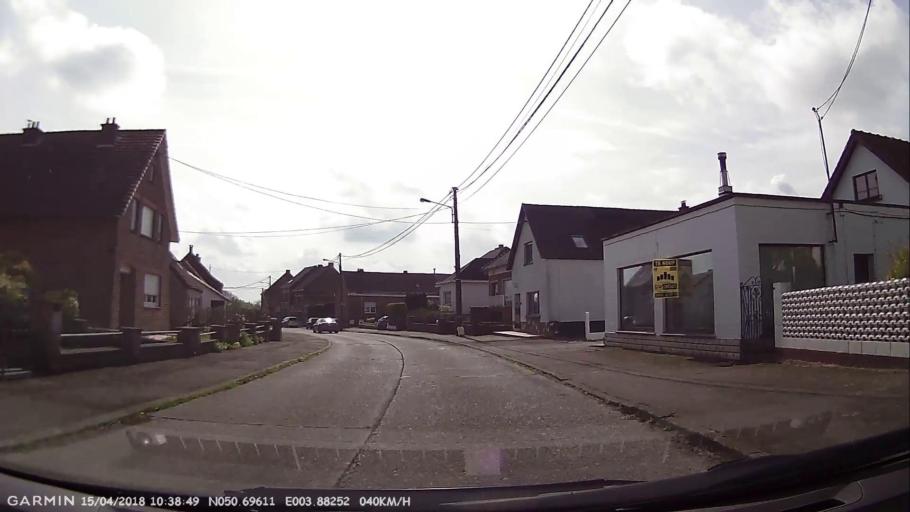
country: BE
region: Wallonia
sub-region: Province du Hainaut
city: Lessines
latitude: 50.6961
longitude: 3.8825
